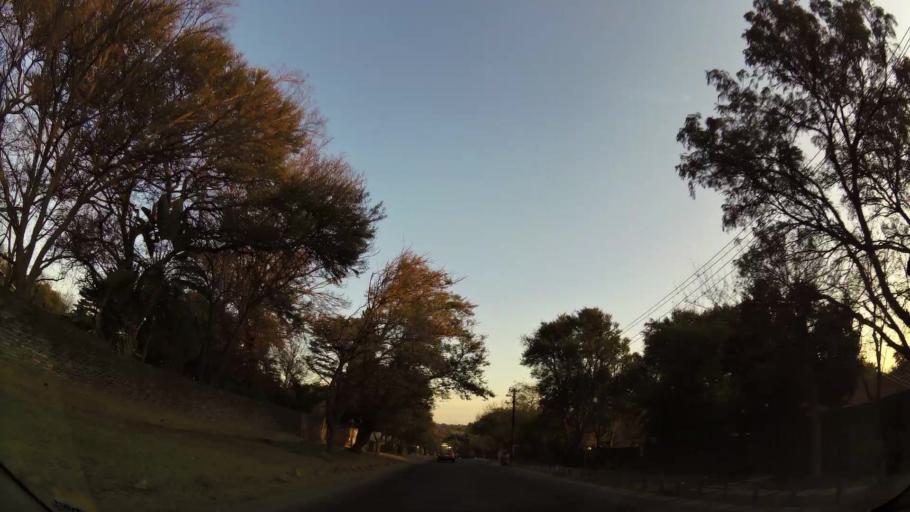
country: ZA
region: Gauteng
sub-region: City of Johannesburg Metropolitan Municipality
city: Johannesburg
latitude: -26.1037
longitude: 27.9946
